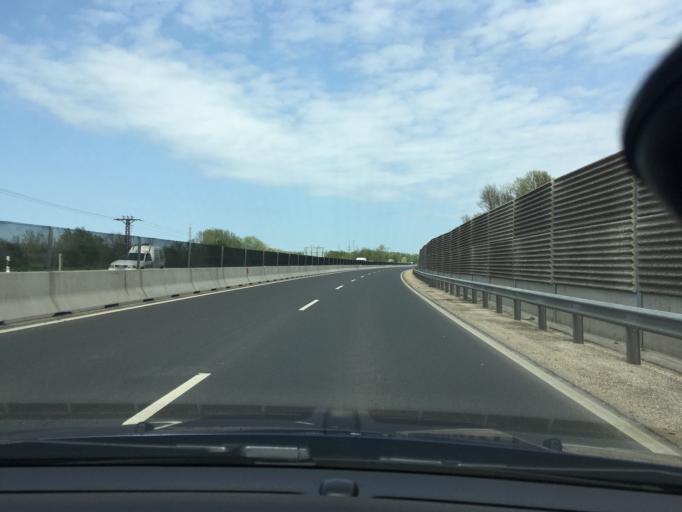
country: HU
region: Csongrad
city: Algyo
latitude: 46.3383
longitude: 20.2006
